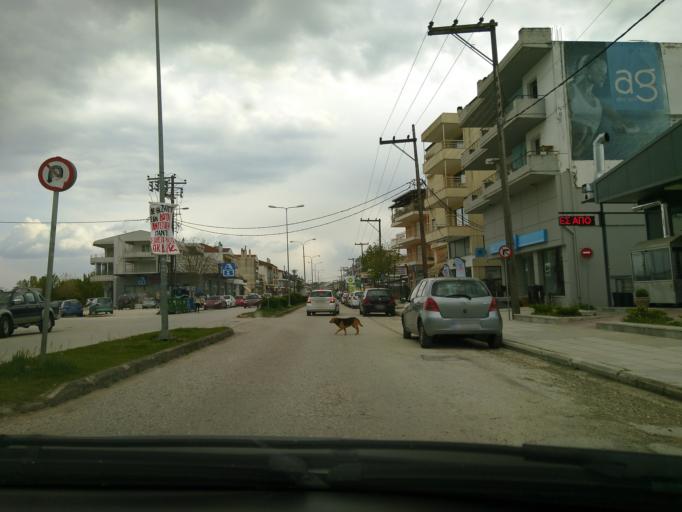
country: GR
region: Epirus
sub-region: Nomos Ioanninon
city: Ioannina
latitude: 39.6613
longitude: 20.8586
